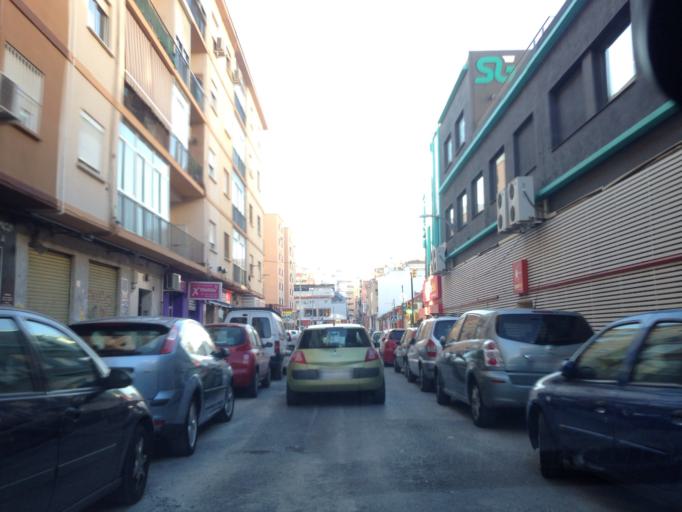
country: ES
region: Andalusia
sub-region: Provincia de Malaga
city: Malaga
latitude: 36.7126
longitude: -4.4377
